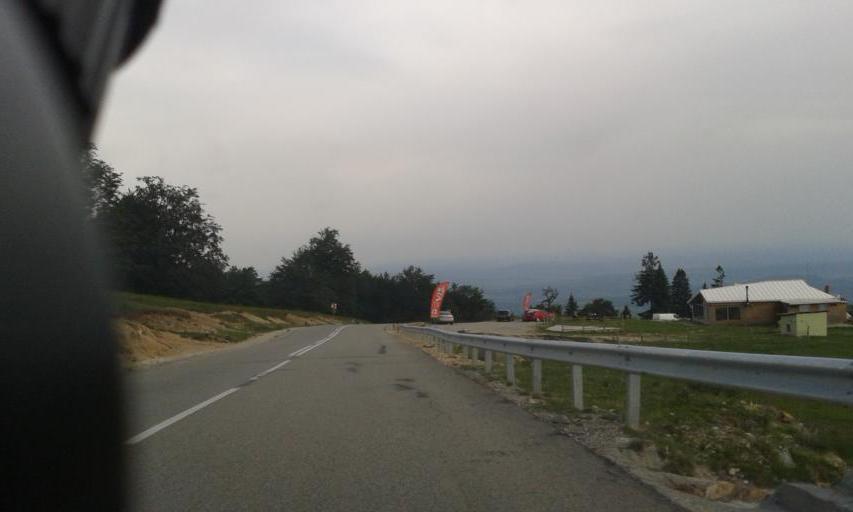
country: RO
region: Gorj
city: Novaci-Straini
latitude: 45.2406
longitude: 23.6963
